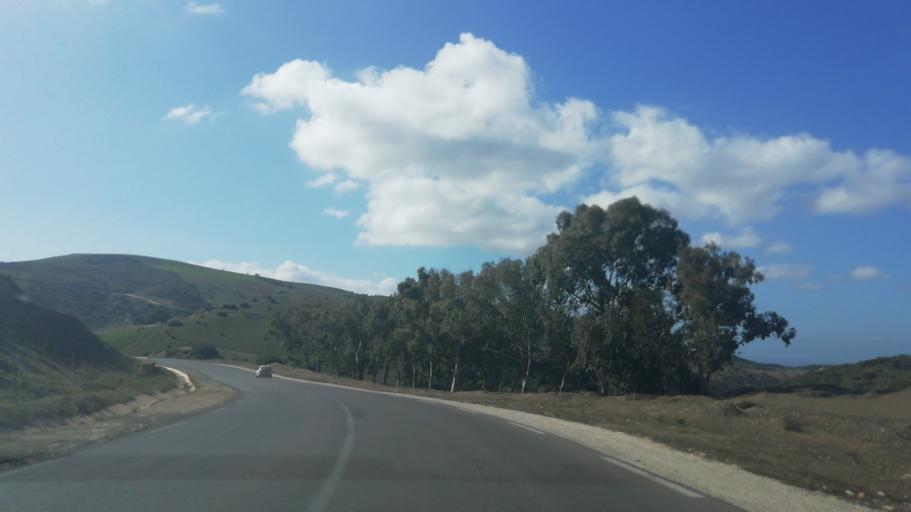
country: DZ
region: Relizane
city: Relizane
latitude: 36.0821
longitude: 0.4879
